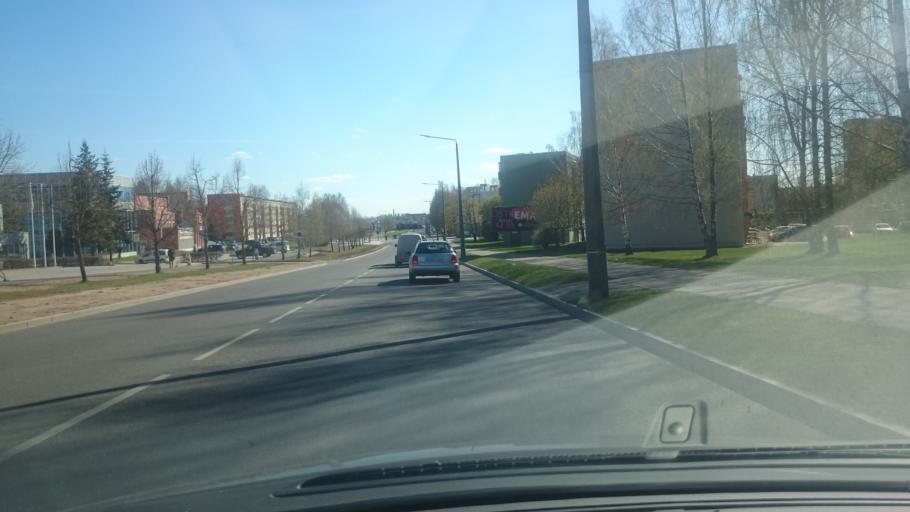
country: EE
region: Tartu
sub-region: Tartu linn
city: Tartu
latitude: 58.3798
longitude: 26.7530
